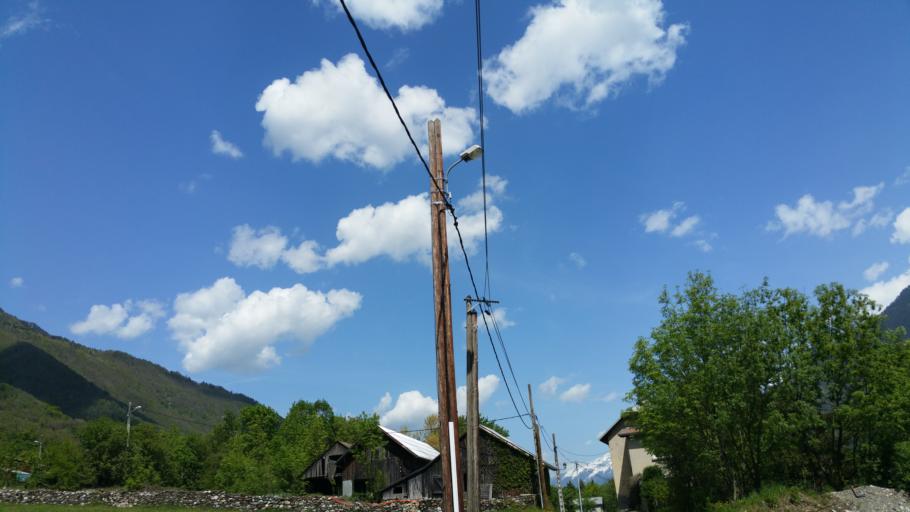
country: FR
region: Rhone-Alpes
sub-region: Departement de la Savoie
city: Saint-Remy-de-Maurienne
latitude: 45.3878
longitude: 6.2628
